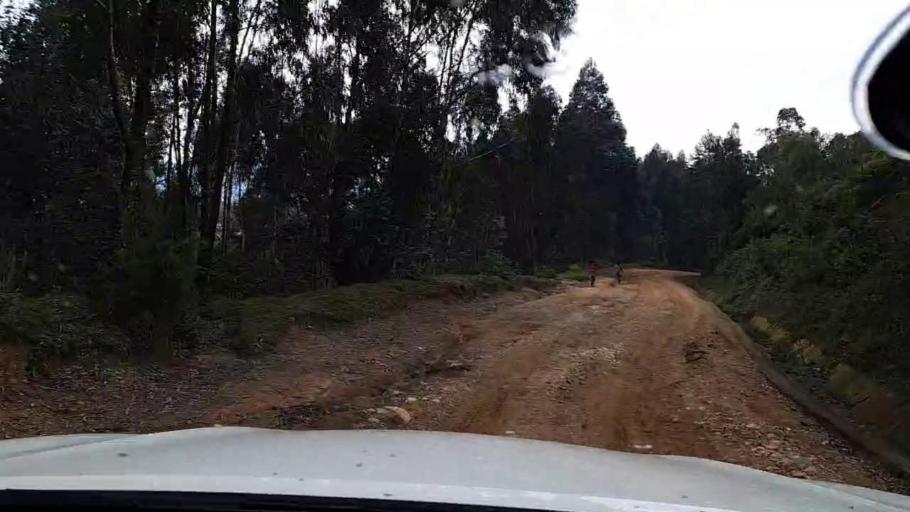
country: RW
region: Western Province
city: Kibuye
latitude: -2.2518
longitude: 29.3464
